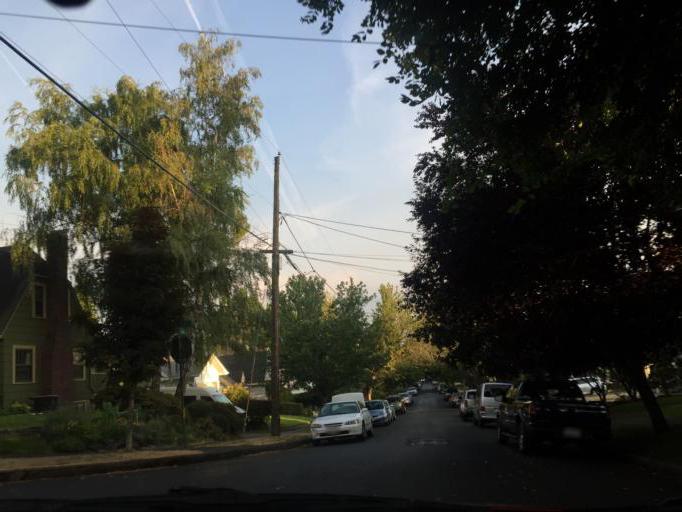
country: US
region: Oregon
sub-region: Multnomah County
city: Portland
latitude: 45.5446
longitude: -122.6240
